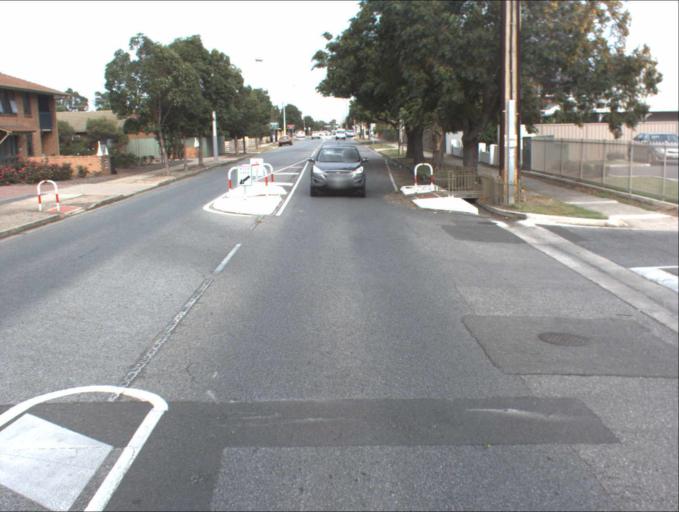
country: AU
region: South Australia
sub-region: Port Adelaide Enfield
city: Birkenhead
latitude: -34.8247
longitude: 138.4905
